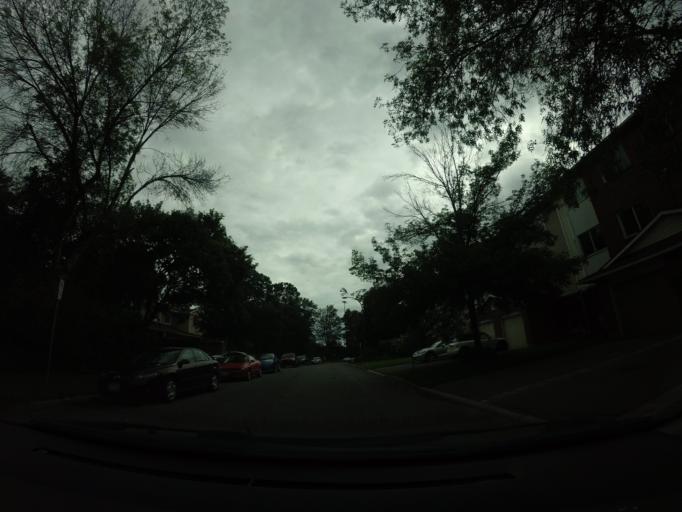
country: CA
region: Quebec
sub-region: Outaouais
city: Gatineau
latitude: 45.4795
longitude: -75.5228
